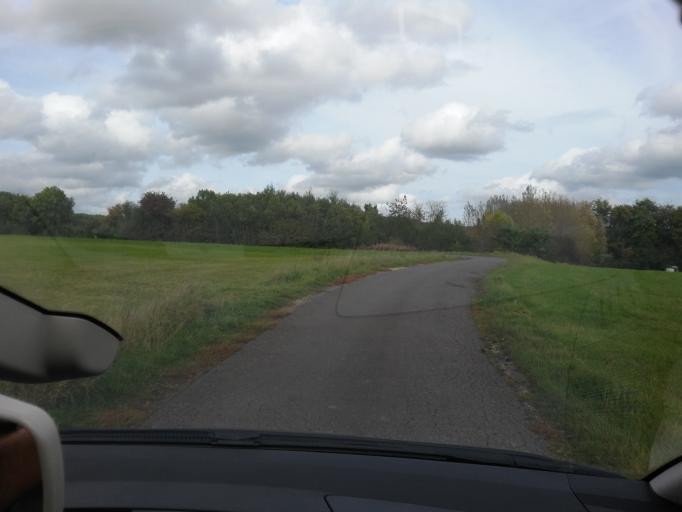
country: BE
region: Wallonia
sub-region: Province du Luxembourg
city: Arlon
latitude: 49.6390
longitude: 5.7801
